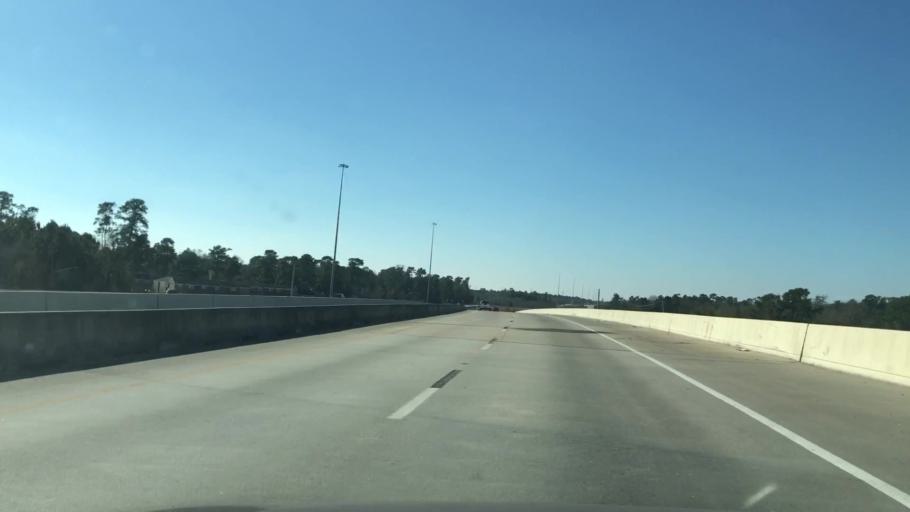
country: US
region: Texas
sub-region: Harris County
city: Cloverleaf
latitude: 29.8169
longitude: -95.2076
